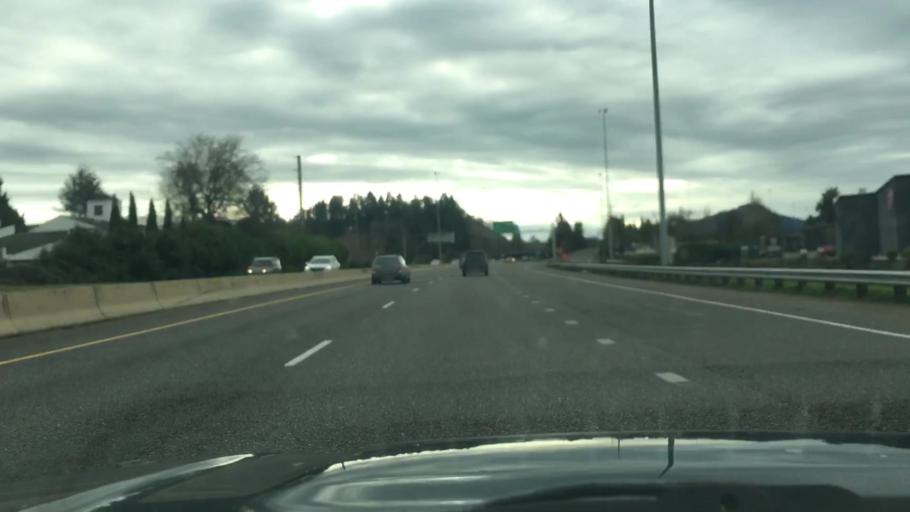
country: US
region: Oregon
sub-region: Lane County
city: Eugene
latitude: 44.0694
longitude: -123.1016
